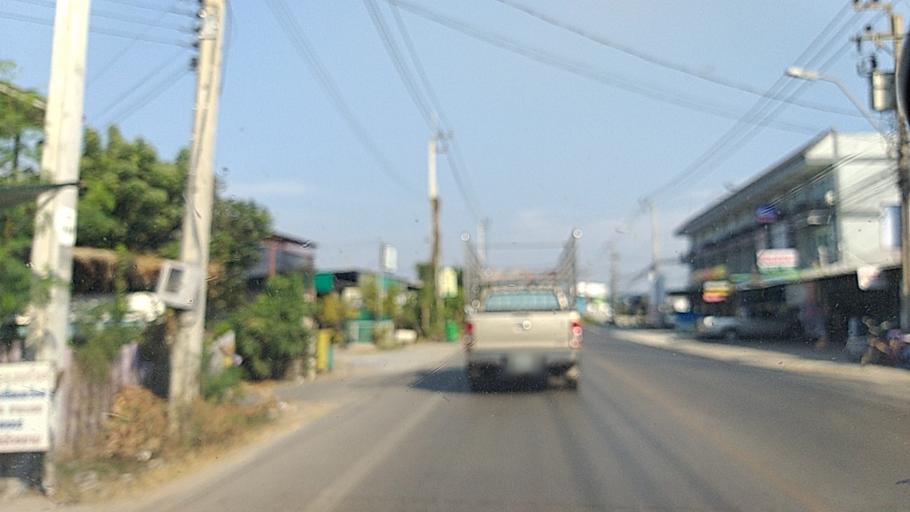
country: TH
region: Nonthaburi
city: Bang Bua Thong
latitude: 13.9385
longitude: 100.3653
